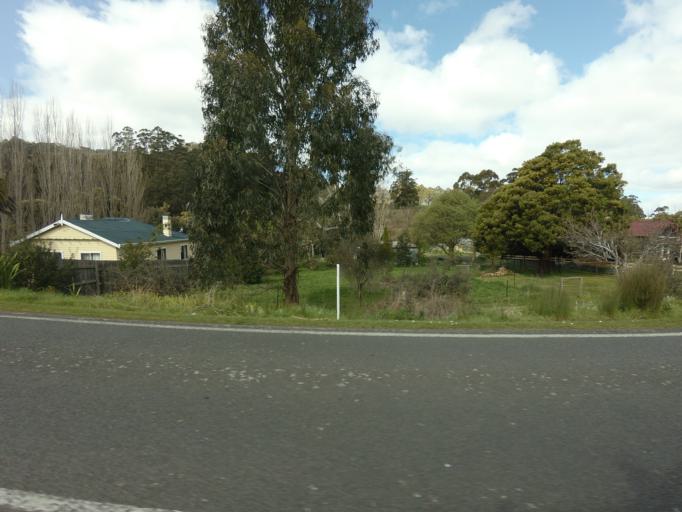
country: AU
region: Tasmania
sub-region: Huon Valley
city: Geeveston
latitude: -43.2997
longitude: 147.0083
